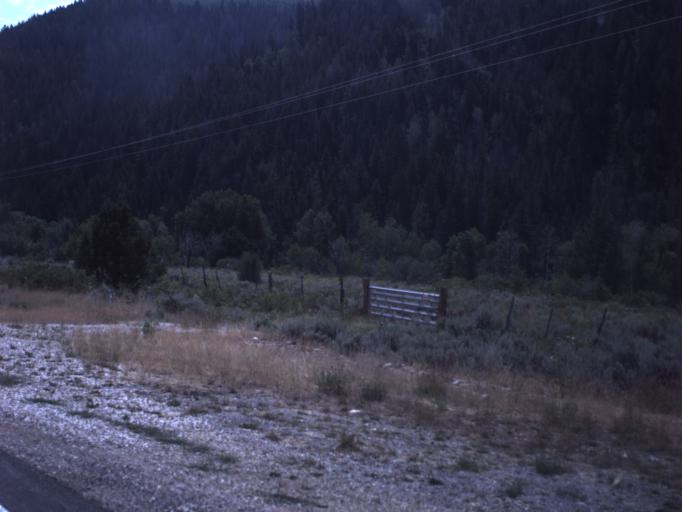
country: US
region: Utah
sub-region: Summit County
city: Francis
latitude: 40.5520
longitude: -111.1592
